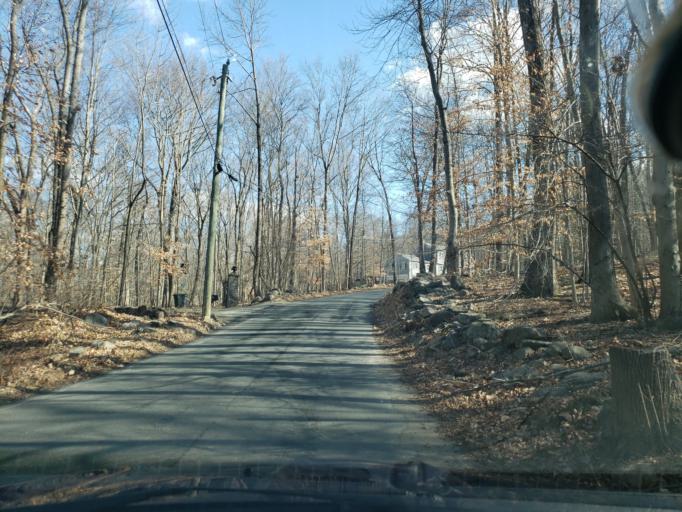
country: US
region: Connecticut
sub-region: Fairfield County
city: Bethel
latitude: 41.3605
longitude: -73.3712
